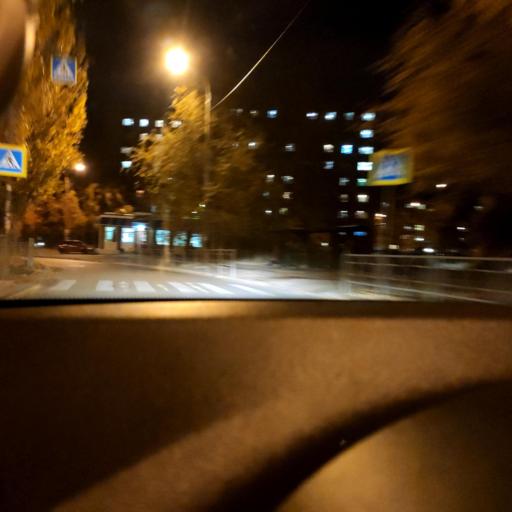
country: RU
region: Samara
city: Samara
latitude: 53.2556
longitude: 50.2386
